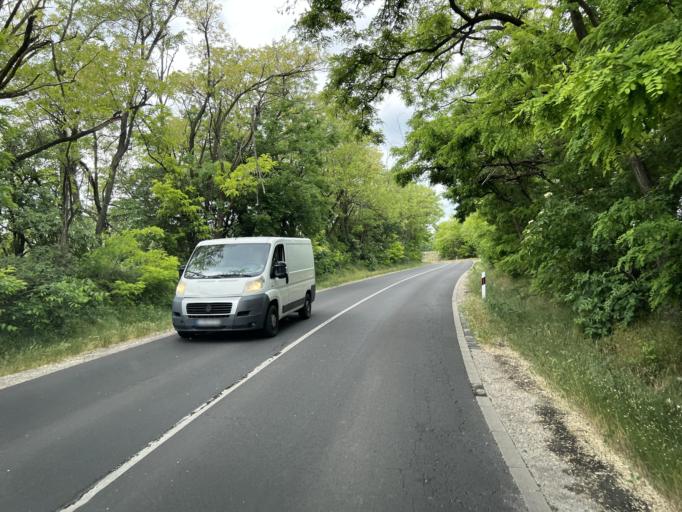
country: HU
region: Pest
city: Pecel
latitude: 47.5270
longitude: 19.3408
